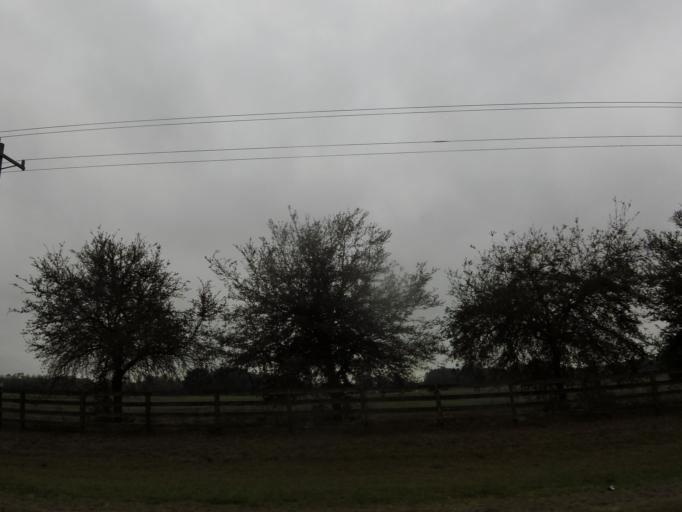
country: US
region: Florida
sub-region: Gilchrist County
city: Trenton
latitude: 29.7958
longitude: -82.8847
